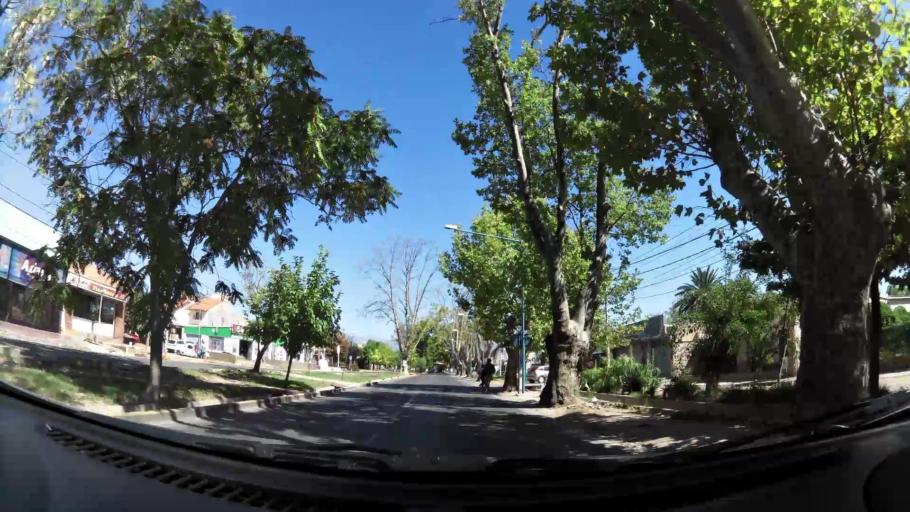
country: AR
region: Mendoza
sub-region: Departamento de Godoy Cruz
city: Godoy Cruz
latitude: -32.9414
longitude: -68.8264
